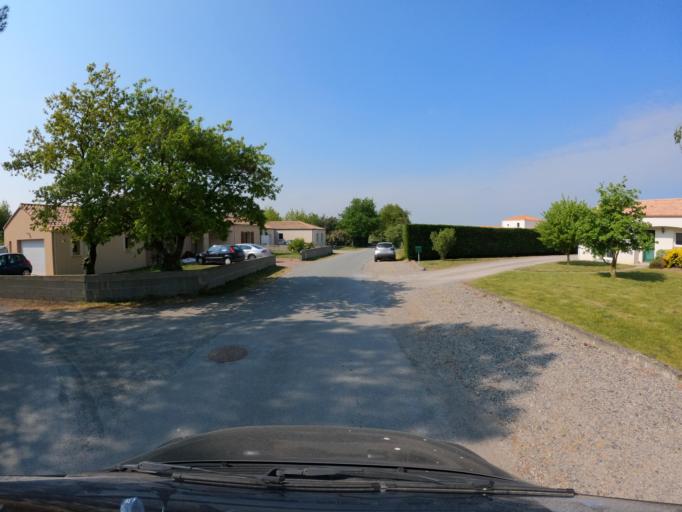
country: FR
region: Pays de la Loire
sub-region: Departement de la Vendee
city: Treize-Septiers
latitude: 46.9999
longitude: -1.2400
